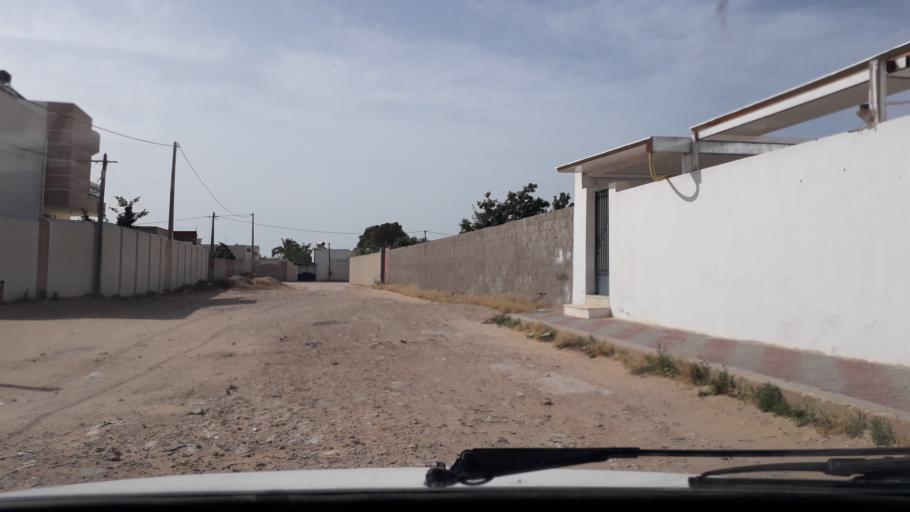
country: TN
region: Safaqis
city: Al Qarmadah
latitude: 34.8082
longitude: 10.7691
